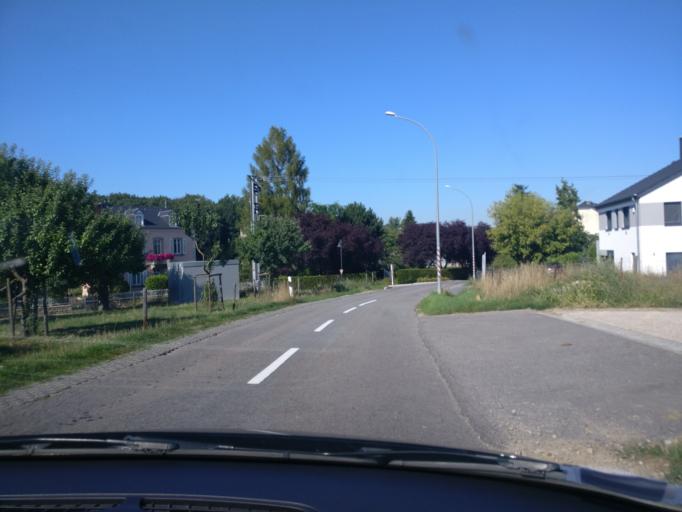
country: LU
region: Grevenmacher
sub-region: Canton d'Echternach
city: Bech
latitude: 49.7278
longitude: 6.3399
